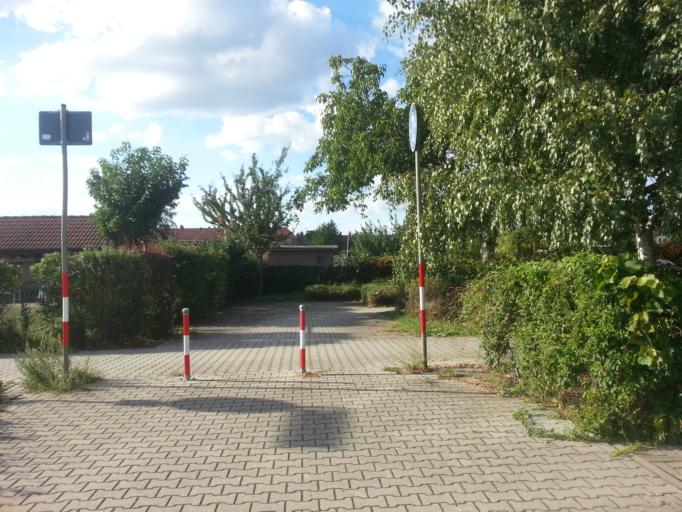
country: DE
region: Baden-Wuerttemberg
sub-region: Karlsruhe Region
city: Ilvesheim
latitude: 49.4610
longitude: 8.5647
